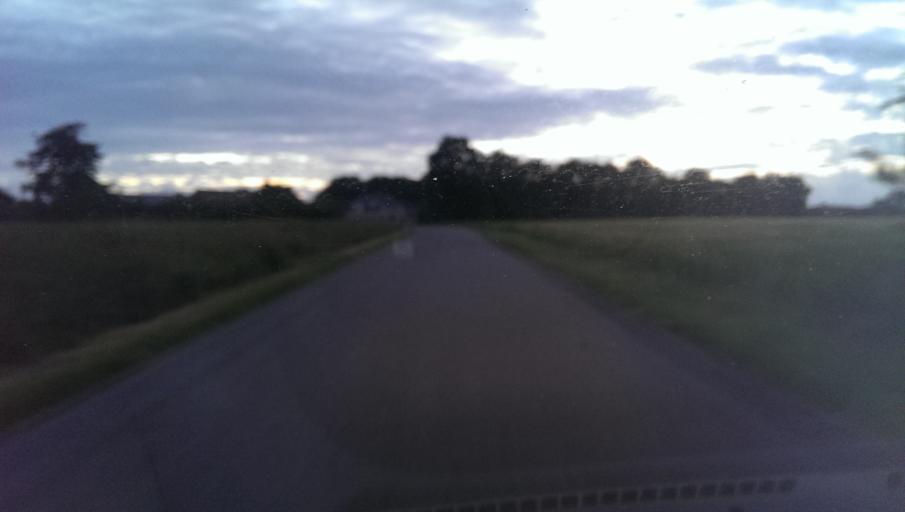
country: DK
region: South Denmark
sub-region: Esbjerg Kommune
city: Esbjerg
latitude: 55.5321
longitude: 8.4844
